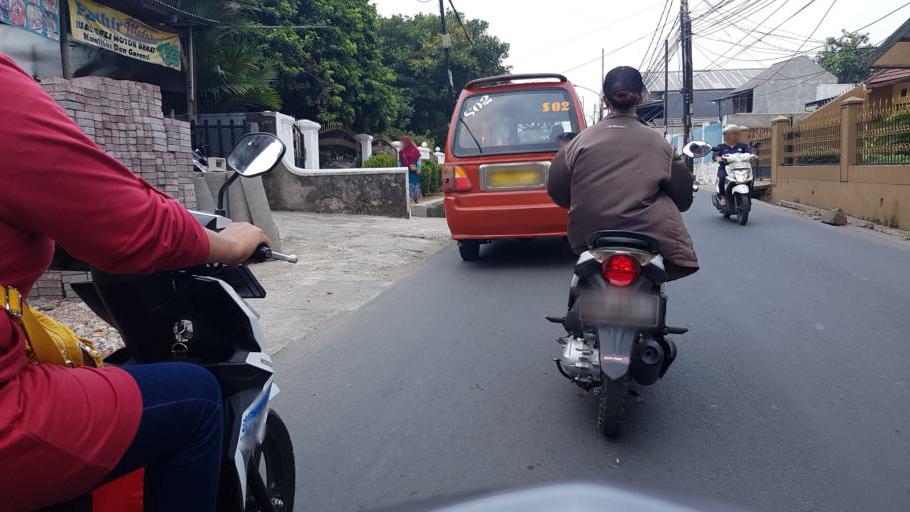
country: ID
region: West Java
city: Bekasi
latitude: -6.2828
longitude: 106.9297
